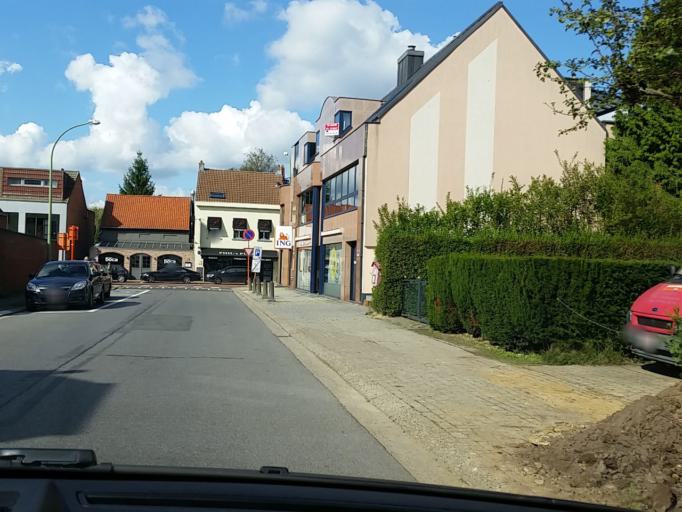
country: BE
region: Flanders
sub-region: Provincie Antwerpen
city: Schilde
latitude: 51.2616
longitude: 4.5512
